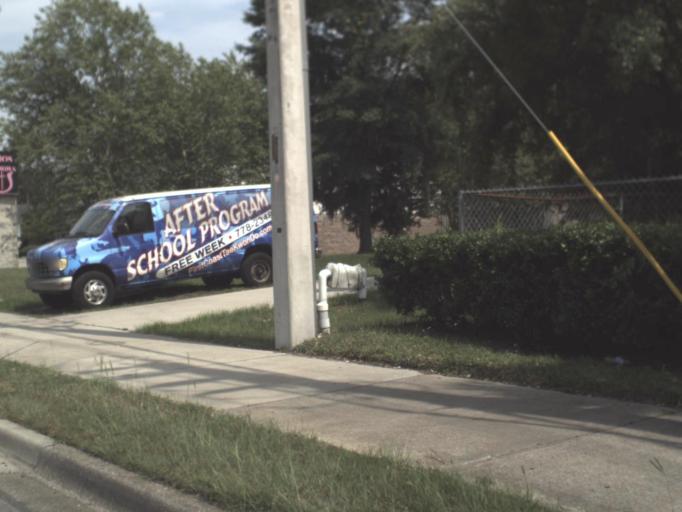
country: US
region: Florida
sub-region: Clay County
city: Bellair-Meadowbrook Terrace
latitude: 30.2482
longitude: -81.7721
